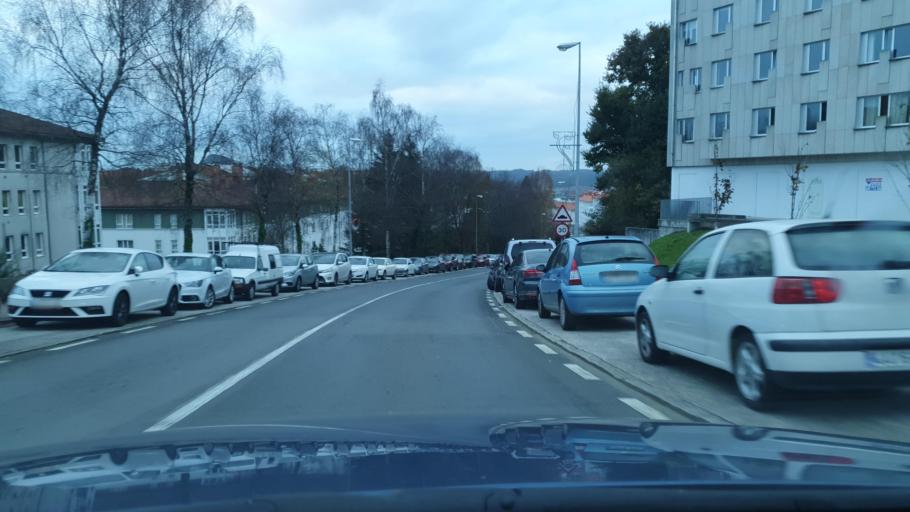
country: ES
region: Galicia
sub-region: Provincia da Coruna
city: Santiago de Compostela
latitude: 42.8854
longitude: -8.5277
